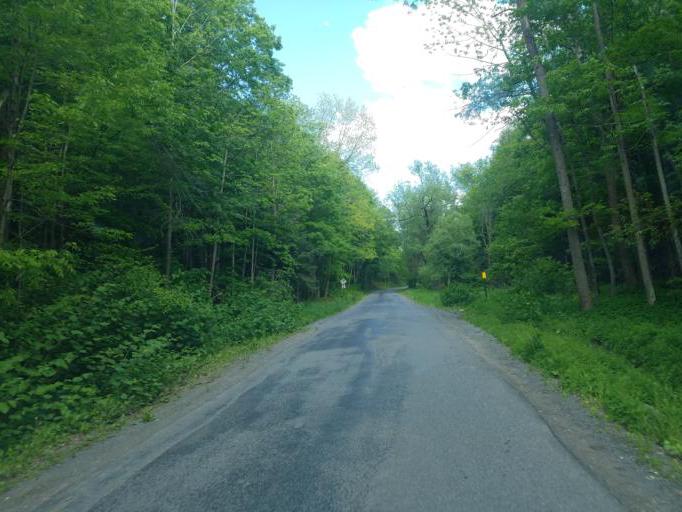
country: US
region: New York
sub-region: Herkimer County
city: Ilion
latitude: 42.9562
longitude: -75.0301
